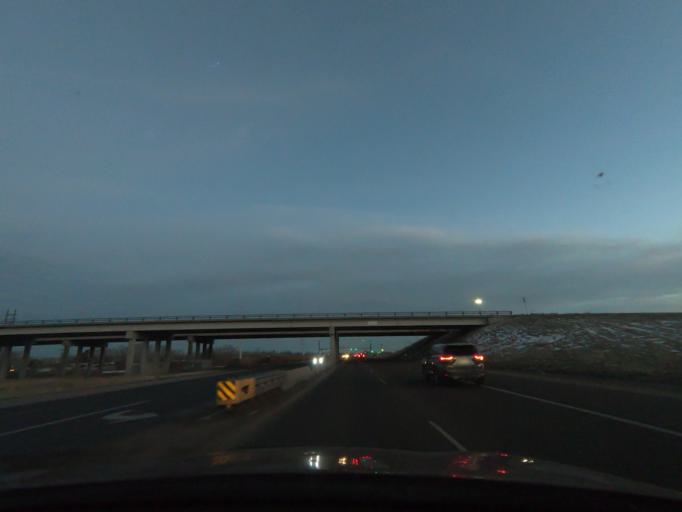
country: US
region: Colorado
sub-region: El Paso County
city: Stratmoor
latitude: 38.7686
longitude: -104.7615
